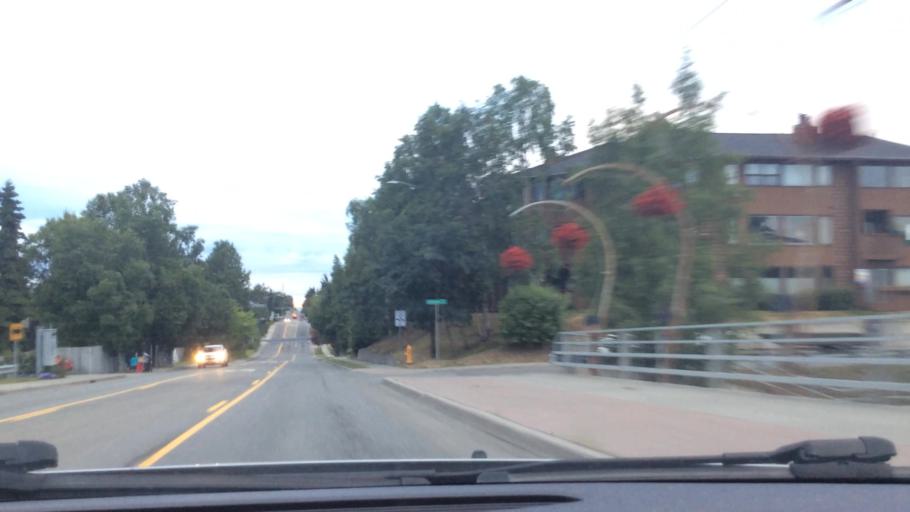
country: US
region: Alaska
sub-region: Anchorage Municipality
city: Anchorage
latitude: 61.2077
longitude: -149.8827
